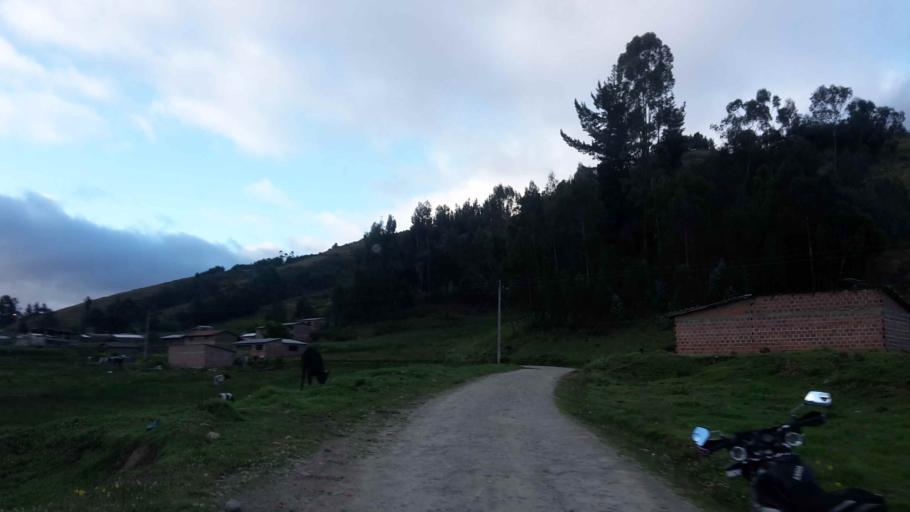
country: BO
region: Cochabamba
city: Colomi
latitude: -17.2740
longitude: -65.9202
